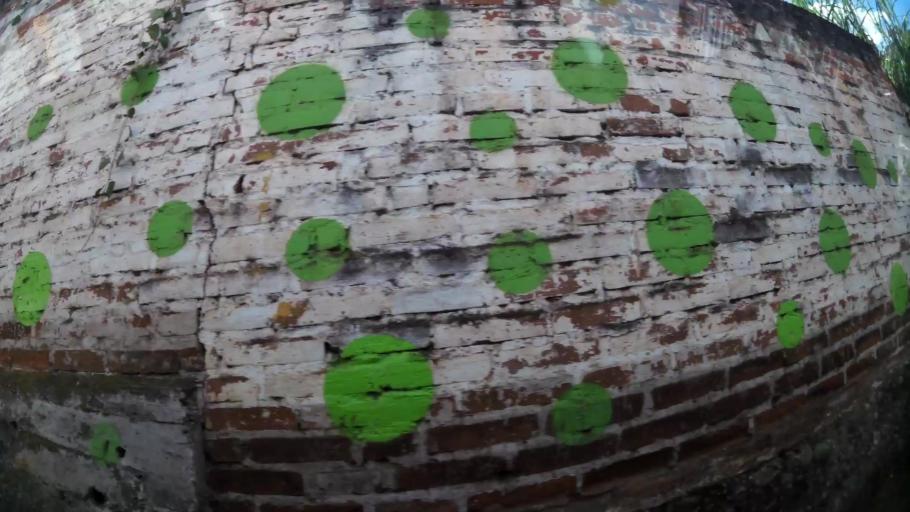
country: CO
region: Antioquia
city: Sabaneta
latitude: 6.1547
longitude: -75.6039
